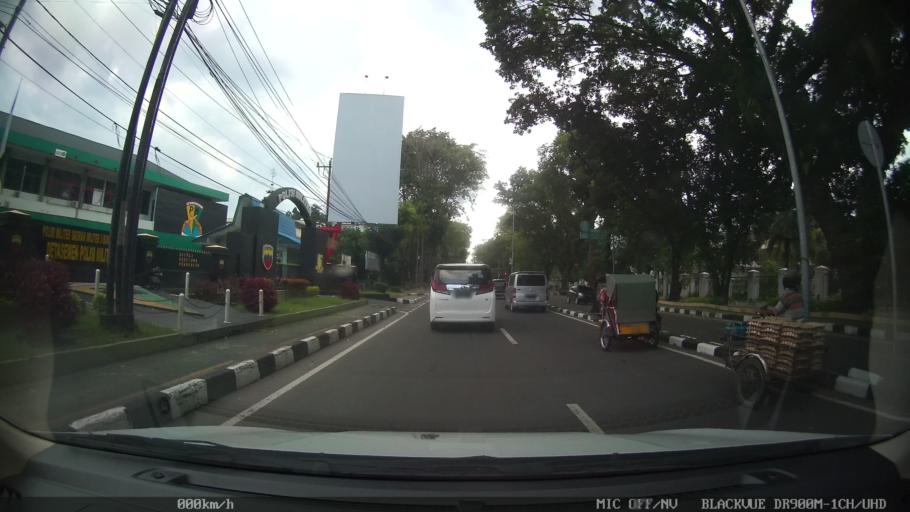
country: ID
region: North Sumatra
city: Medan
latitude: 3.5795
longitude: 98.6794
